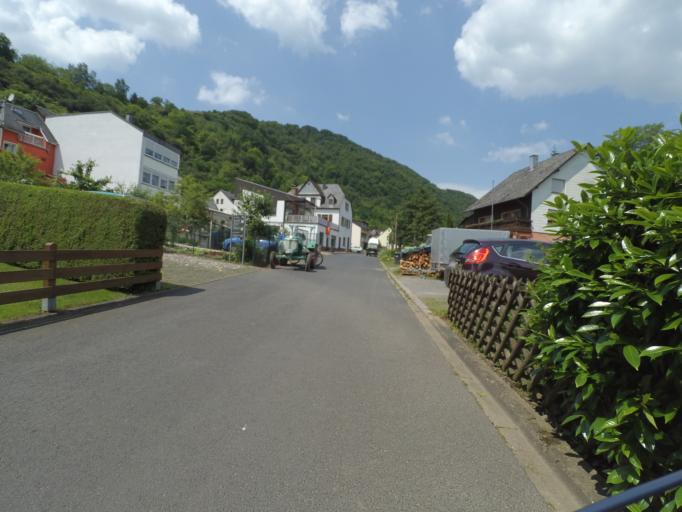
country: DE
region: Rheinland-Pfalz
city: Pommern
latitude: 50.1709
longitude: 7.2734
